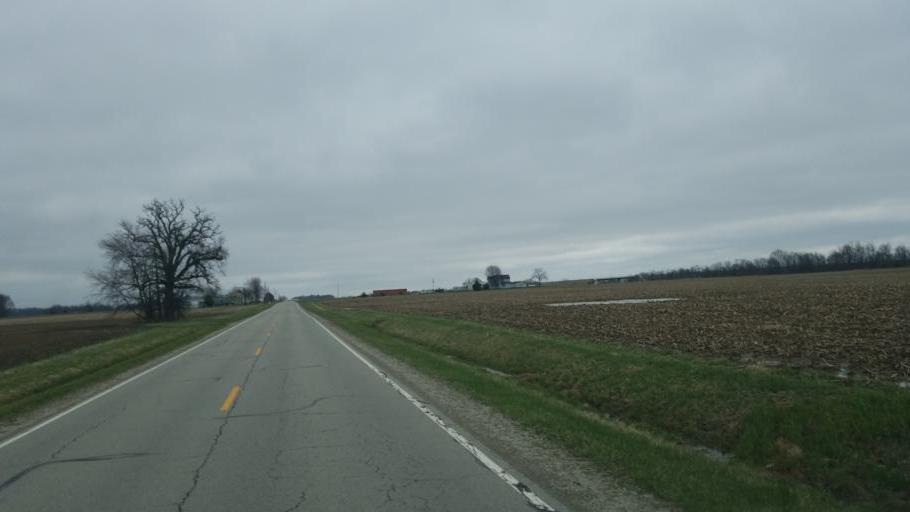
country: US
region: Ohio
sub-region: Crawford County
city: Bucyrus
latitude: 40.8191
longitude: -83.1059
